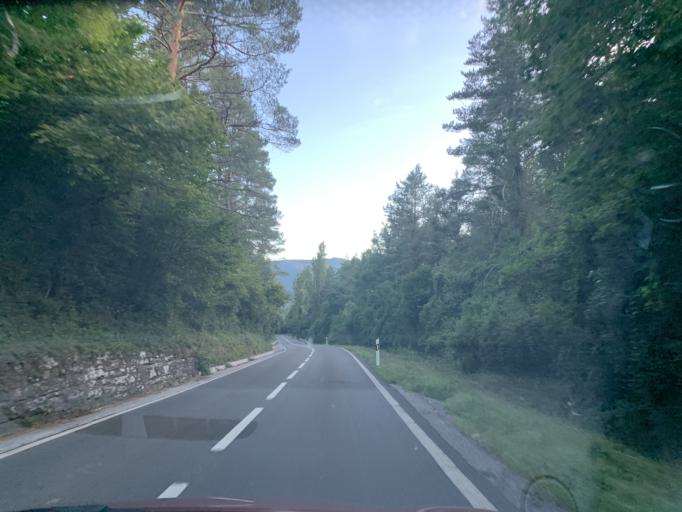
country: ES
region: Aragon
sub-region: Provincia de Huesca
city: Broto
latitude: 42.5648
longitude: -0.1146
